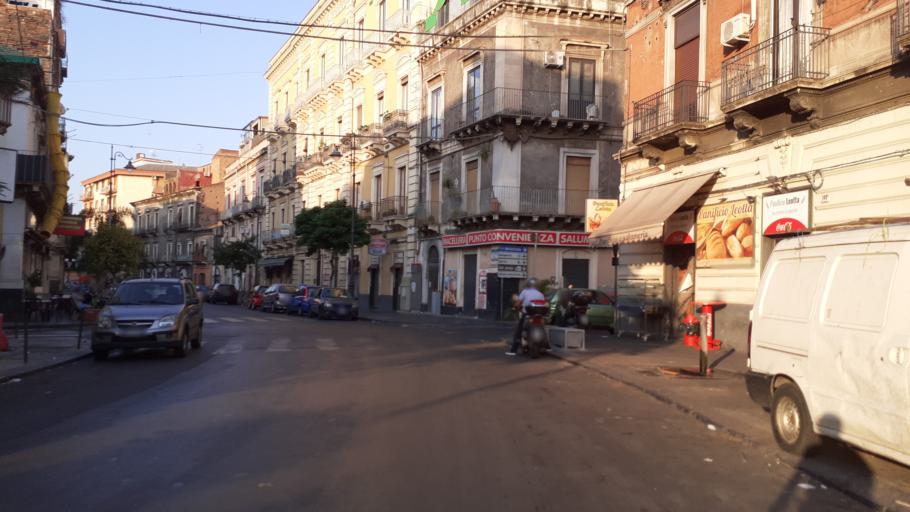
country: IT
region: Sicily
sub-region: Catania
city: Catania
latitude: 37.4975
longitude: 15.0846
